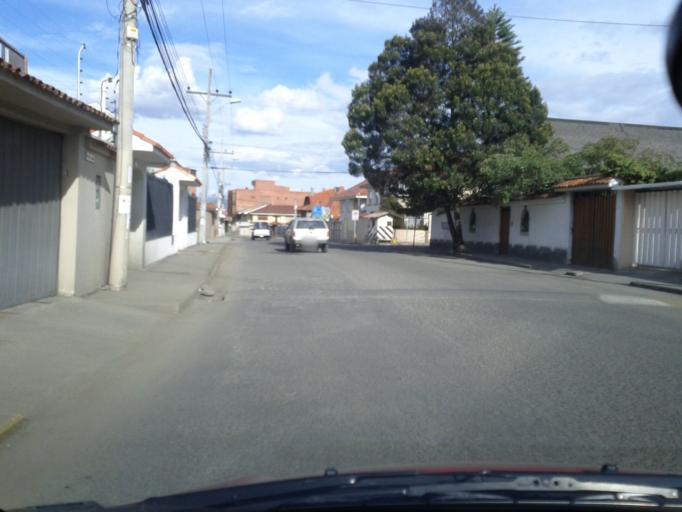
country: EC
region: Azuay
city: Cuenca
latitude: -2.8930
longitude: -79.0300
